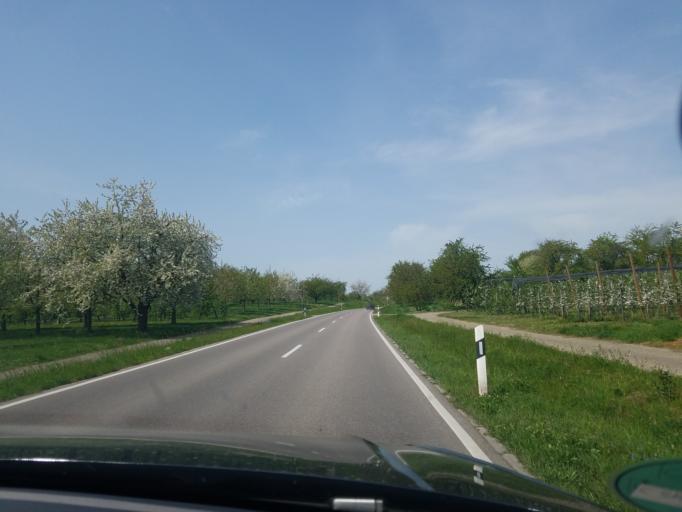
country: DE
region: Baden-Wuerttemberg
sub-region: Freiburg Region
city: Haslach
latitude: 48.5708
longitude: 8.0531
